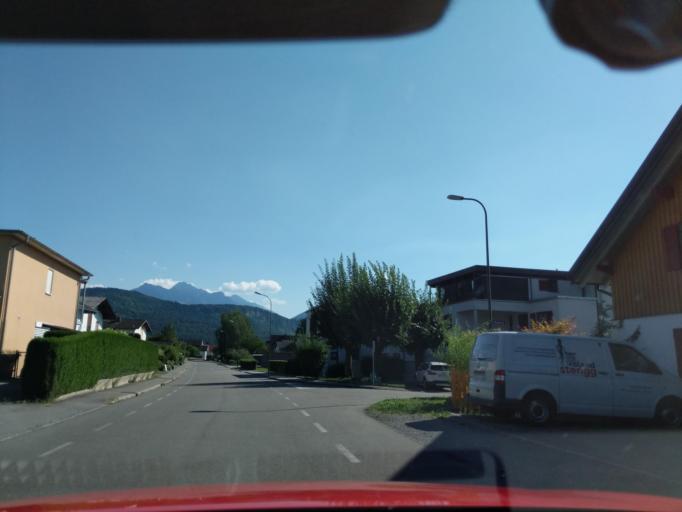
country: AT
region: Vorarlberg
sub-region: Politischer Bezirk Feldkirch
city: Rankweil
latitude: 47.2766
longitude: 9.6308
